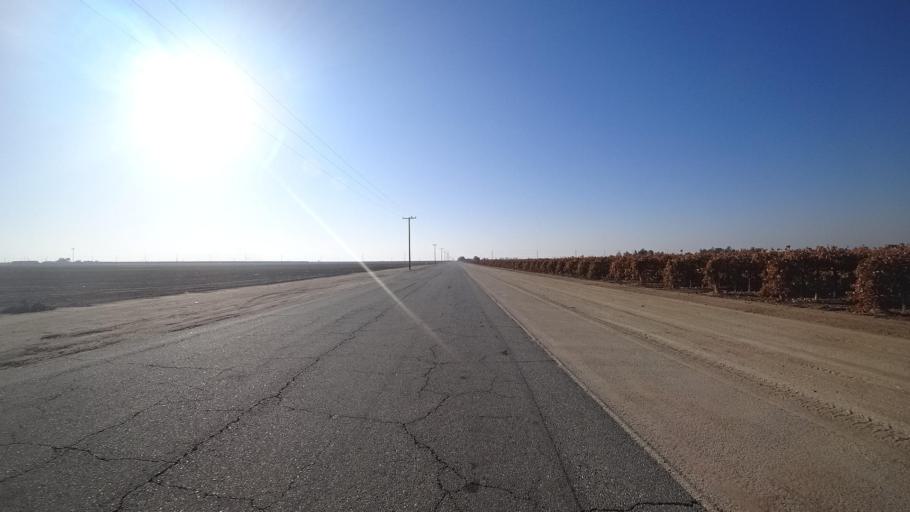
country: US
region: California
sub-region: Tulare County
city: Richgrove
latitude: 35.7814
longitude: -119.1697
